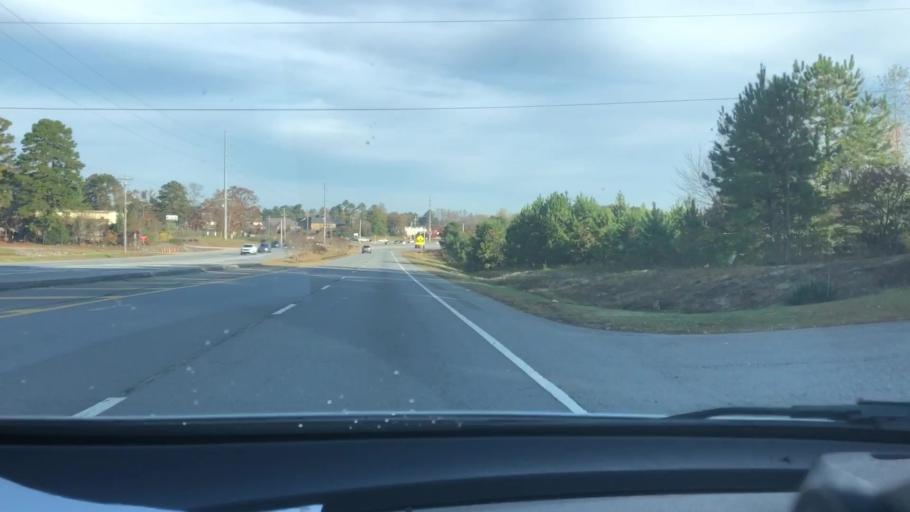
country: US
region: Georgia
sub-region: Fulton County
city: Johns Creek
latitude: 34.1126
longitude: -84.1764
